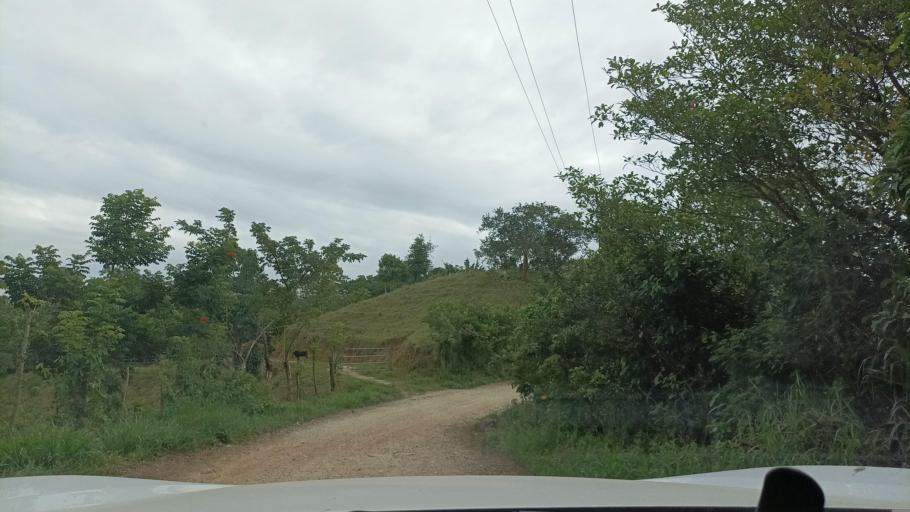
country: MX
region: Veracruz
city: Hidalgotitlan
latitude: 17.6062
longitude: -94.4296
